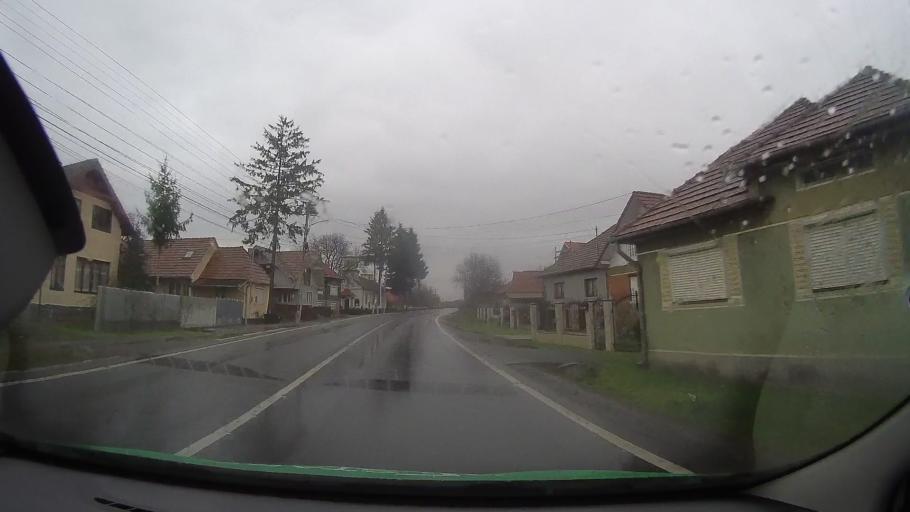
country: RO
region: Mures
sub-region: Comuna Alunis
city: Alunis
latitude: 46.8930
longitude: 24.8006
